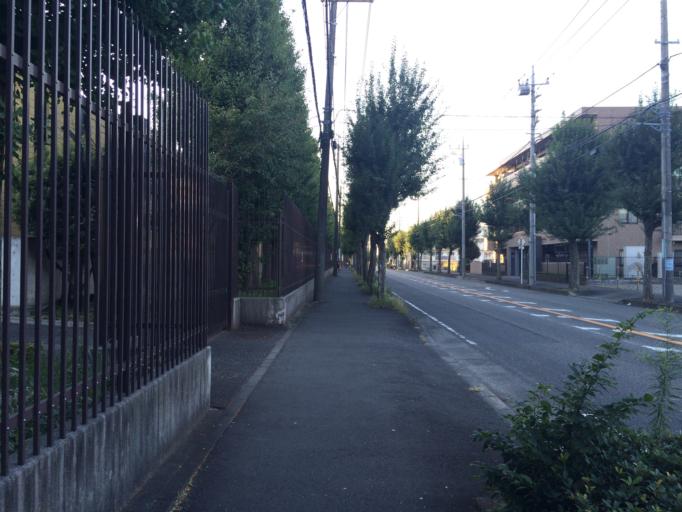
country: JP
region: Tokyo
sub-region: Machida-shi
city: Machida
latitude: 35.5672
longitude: 139.4052
